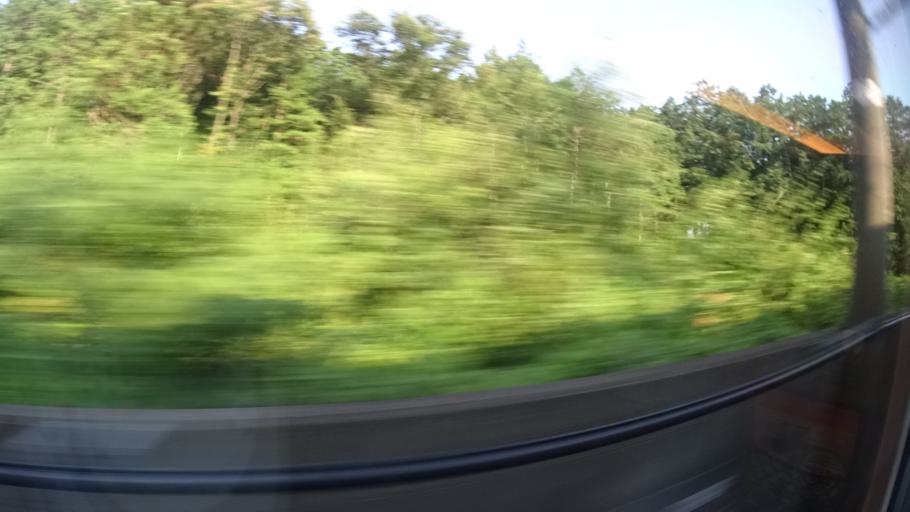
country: JP
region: Tochigi
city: Yaita
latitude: 36.7936
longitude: 139.9548
